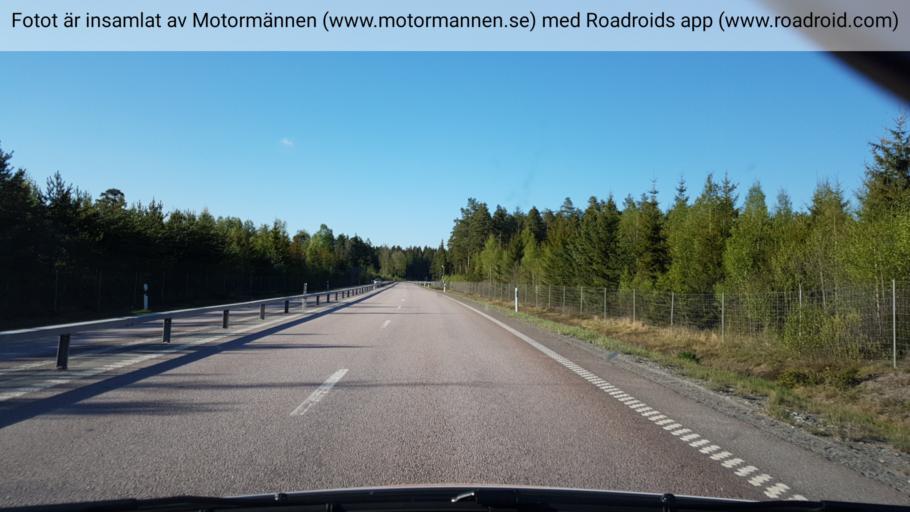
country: SE
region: Vaestmanland
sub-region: Vasteras
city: Tillberga
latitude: 59.7700
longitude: 16.5617
